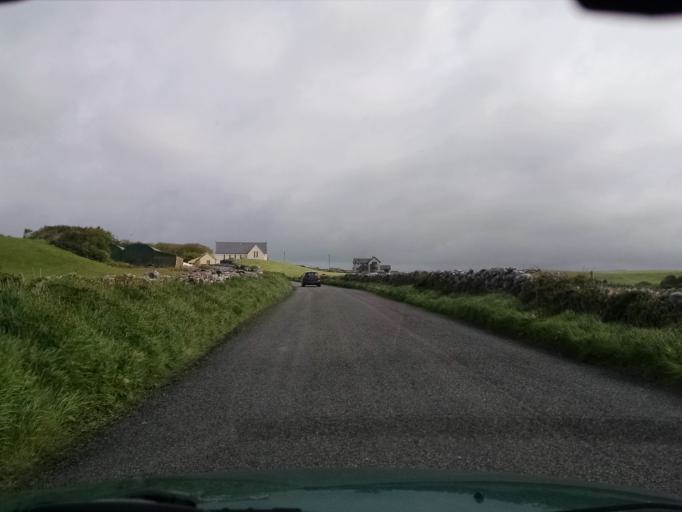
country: IE
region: Connaught
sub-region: County Galway
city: Bearna
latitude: 53.0228
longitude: -9.3685
